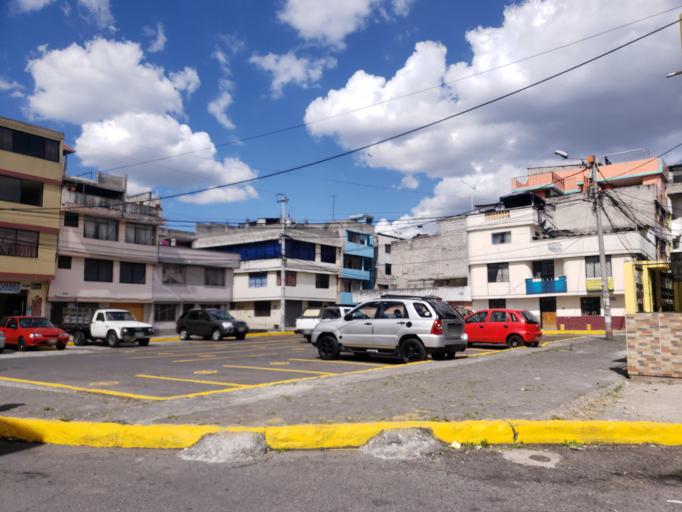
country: EC
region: Pichincha
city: Quito
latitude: -0.2729
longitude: -78.5399
